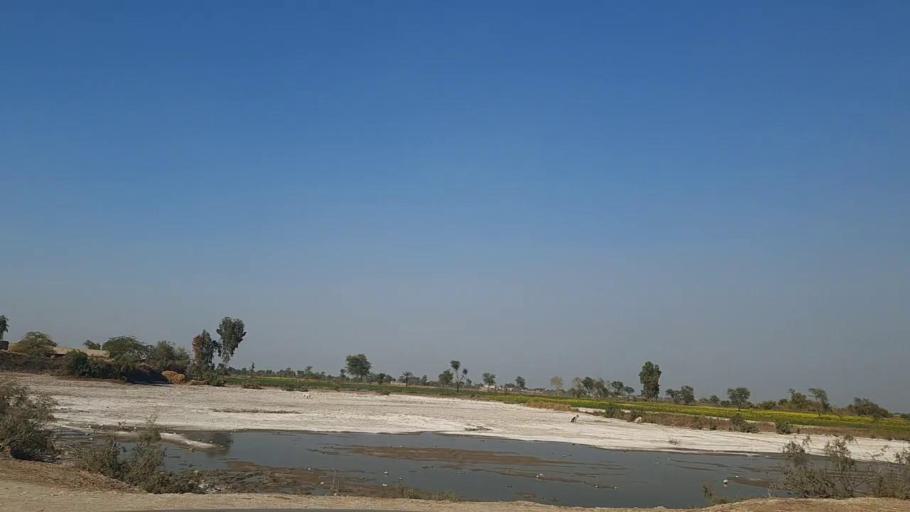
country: PK
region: Sindh
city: Daur
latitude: 26.3178
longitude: 68.1786
